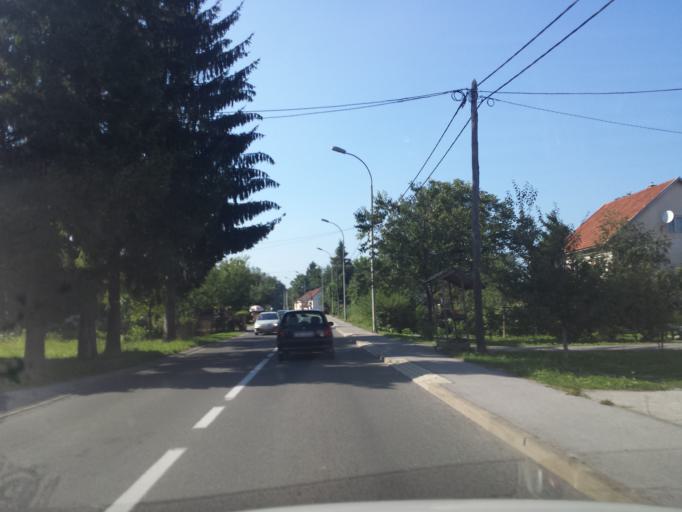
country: HR
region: Karlovacka
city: Ostarije
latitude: 45.2346
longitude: 15.2558
